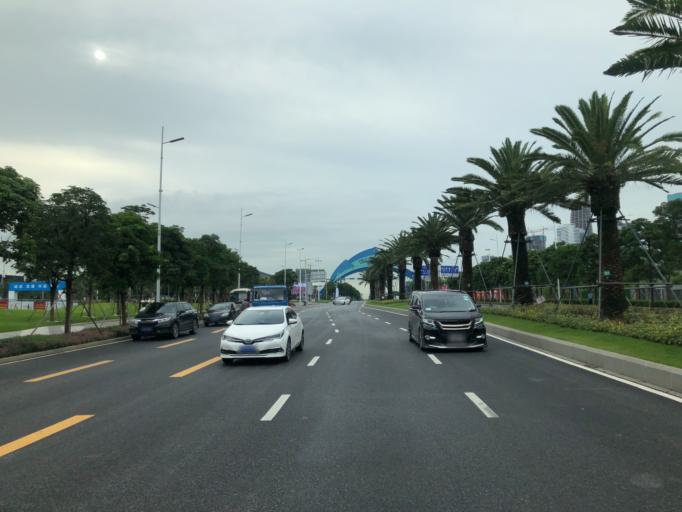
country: CN
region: Guangdong
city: Nantou
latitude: 22.5194
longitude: 113.9003
